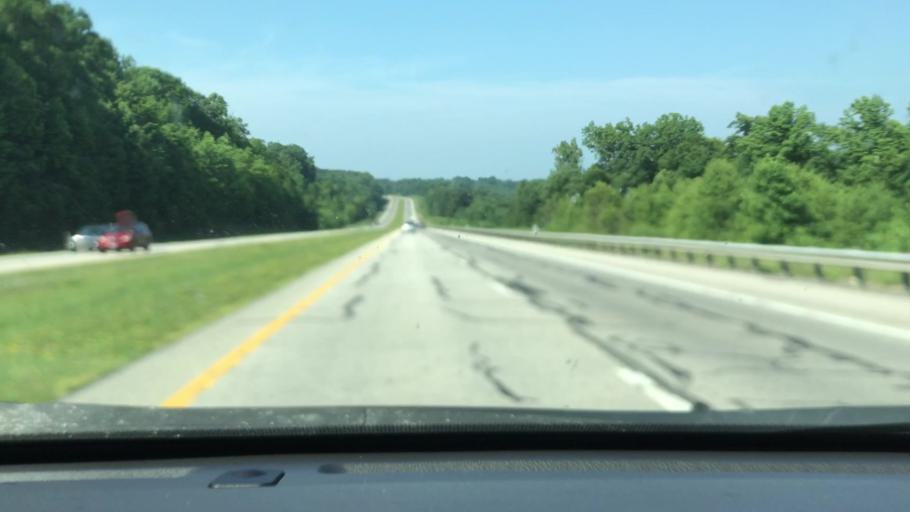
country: US
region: West Virginia
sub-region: Nicholas County
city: Summersville
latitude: 38.1886
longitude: -80.8761
